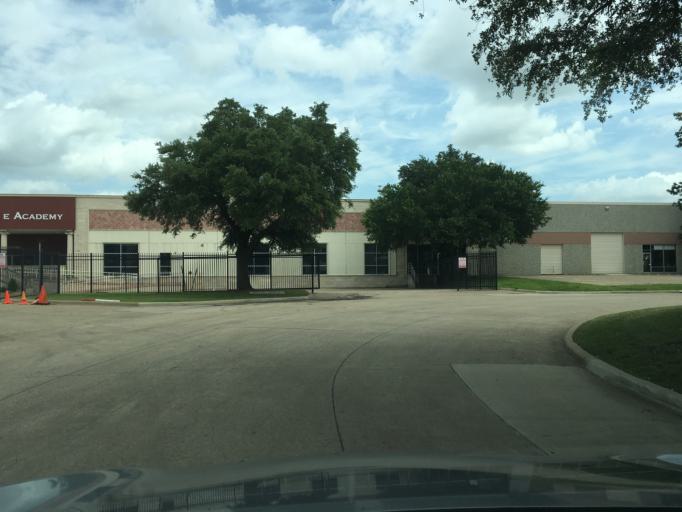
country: US
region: Texas
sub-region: Dallas County
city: Richardson
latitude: 32.9120
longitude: -96.7043
